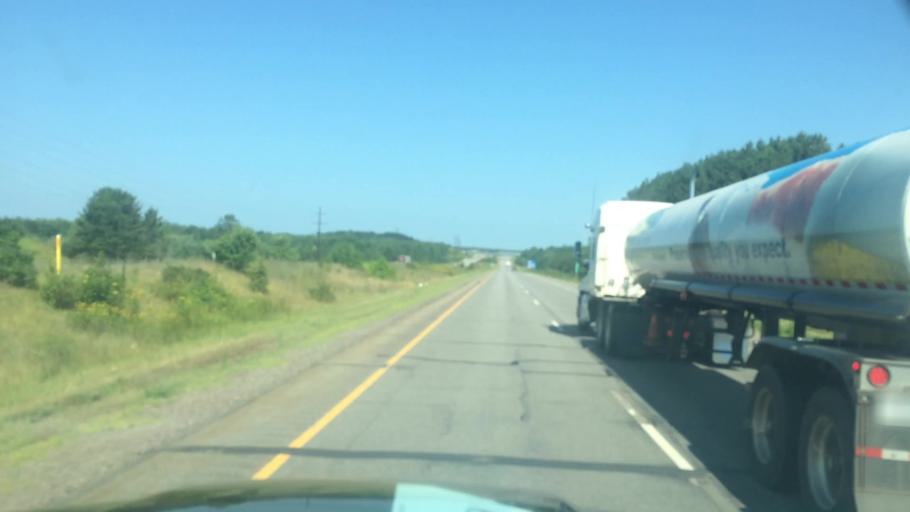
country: US
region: Wisconsin
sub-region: Lincoln County
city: Merrill
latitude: 45.1995
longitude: -89.6516
